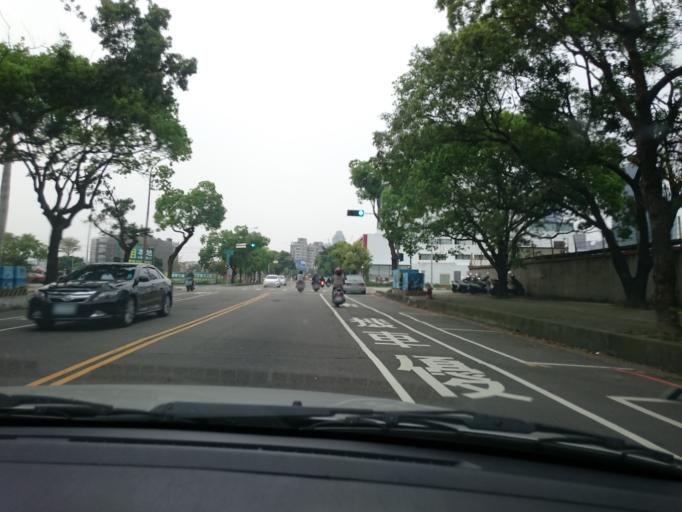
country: TW
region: Taiwan
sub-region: Taichung City
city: Taichung
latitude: 24.1579
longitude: 120.6342
